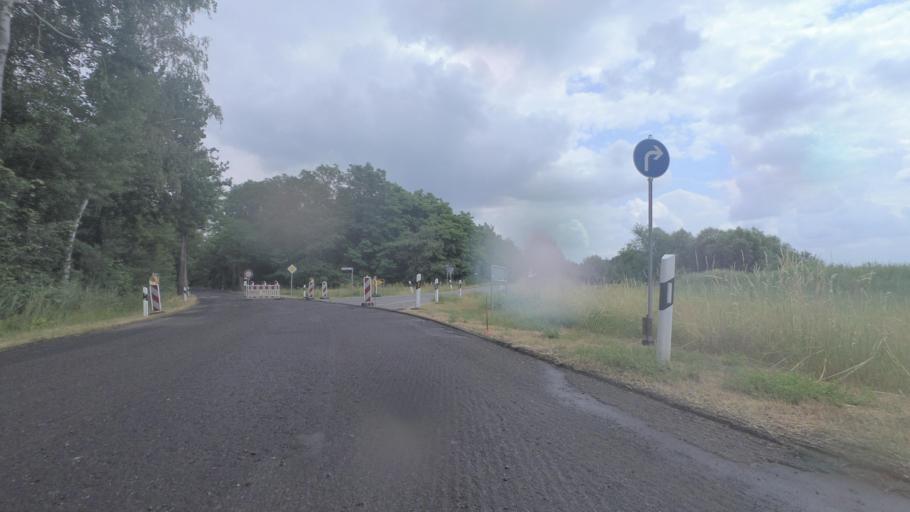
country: DE
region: Brandenburg
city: Sperenberg
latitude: 52.1331
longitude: 13.3785
